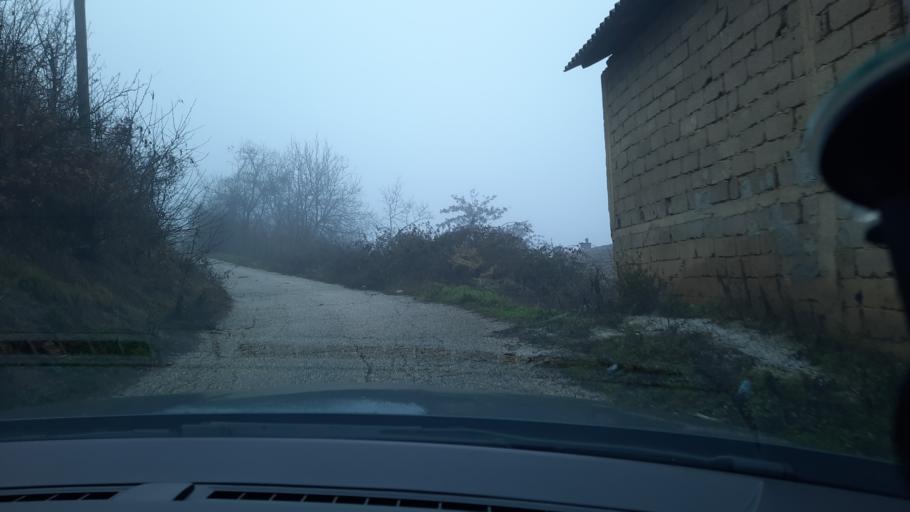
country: MK
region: Vrapciste
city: Vrapciste
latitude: 41.8400
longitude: 20.8801
